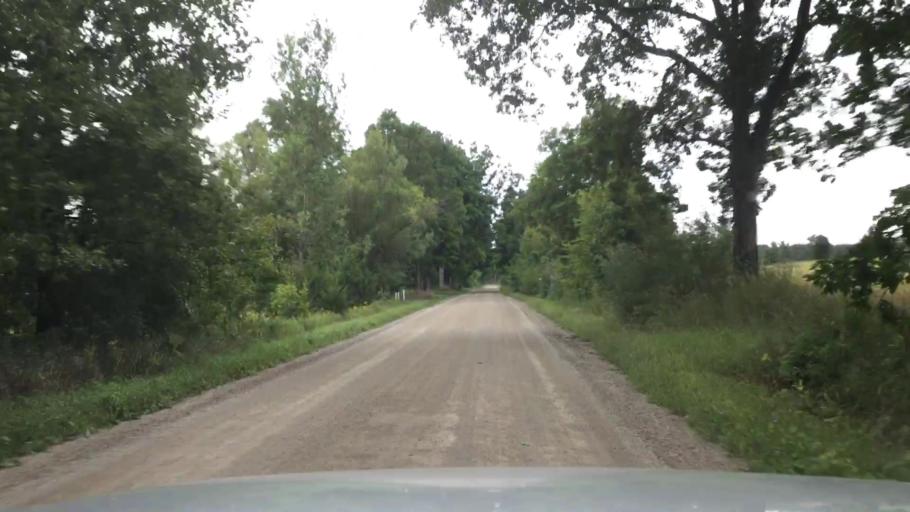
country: US
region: Michigan
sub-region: Shiawassee County
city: Corunna
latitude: 42.9310
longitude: -84.1047
